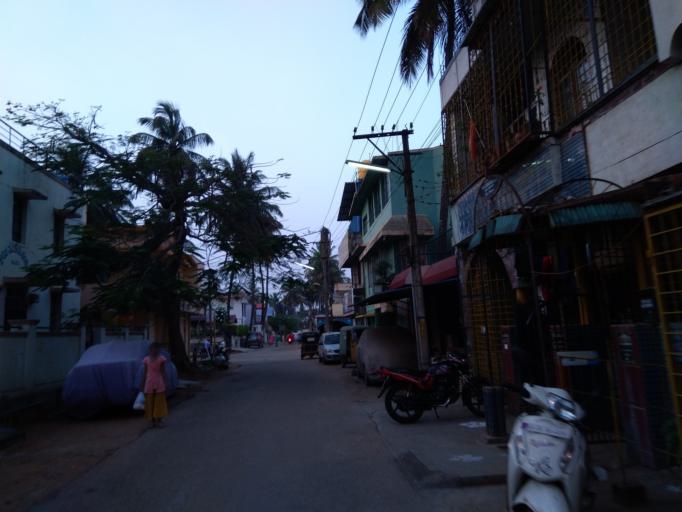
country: IN
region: Karnataka
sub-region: Hassan
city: Hassan
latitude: 13.0115
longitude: 76.1090
